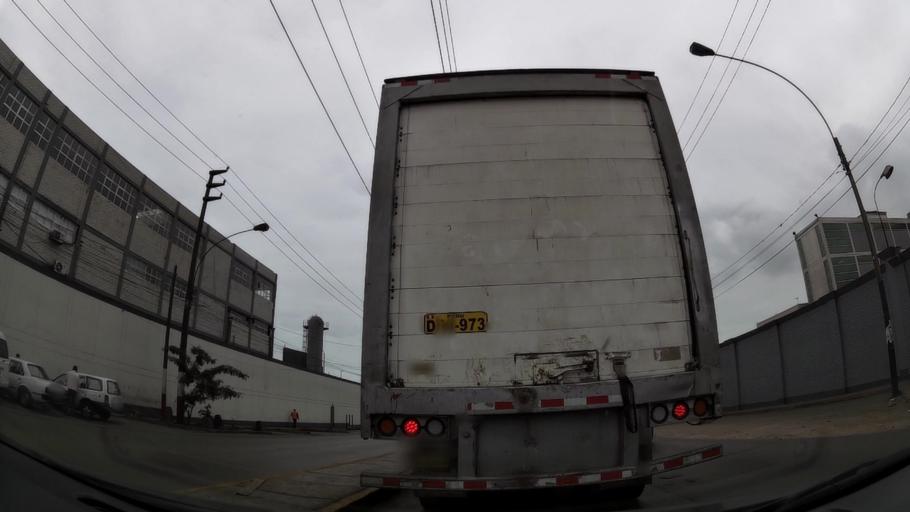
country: PE
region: Callao
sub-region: Callao
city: Callao
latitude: -12.0483
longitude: -77.0972
